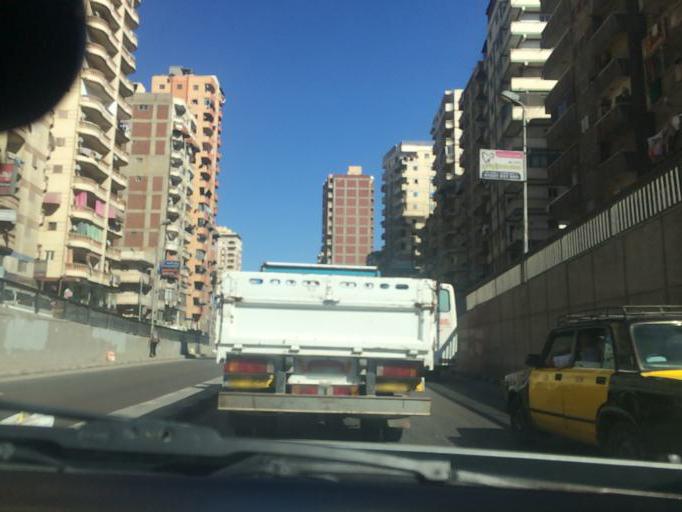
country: EG
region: Alexandria
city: Alexandria
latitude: 31.2661
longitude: 30.0022
